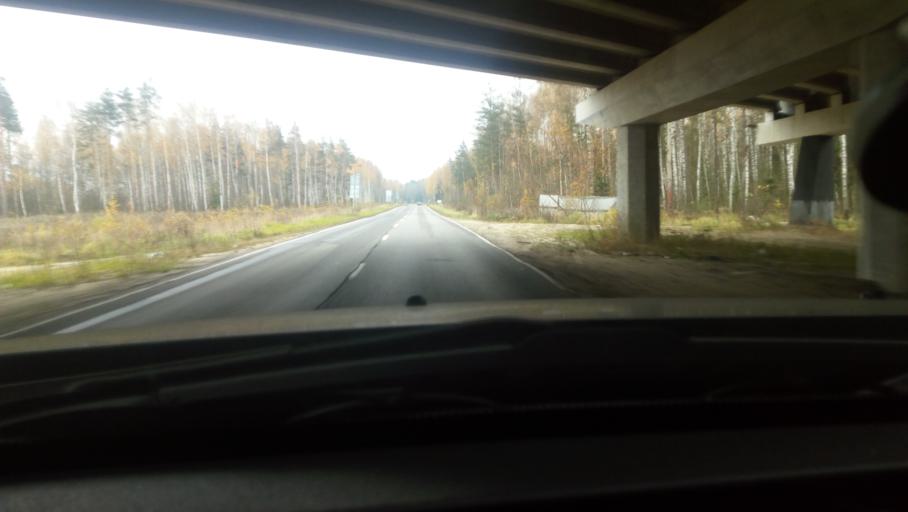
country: RU
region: Moskovskaya
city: Likino-Dulevo
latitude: 55.6992
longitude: 38.8926
